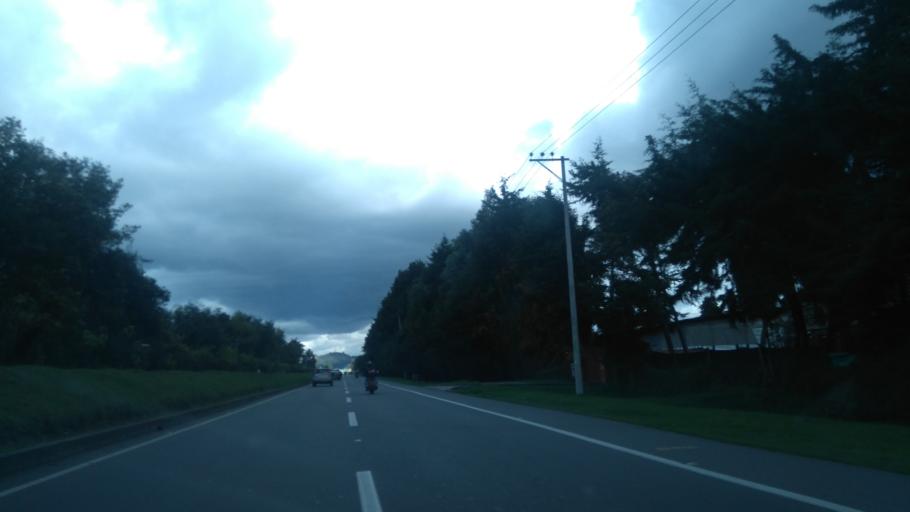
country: CO
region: Cundinamarca
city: El Rosal
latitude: 4.8304
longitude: -74.2448
